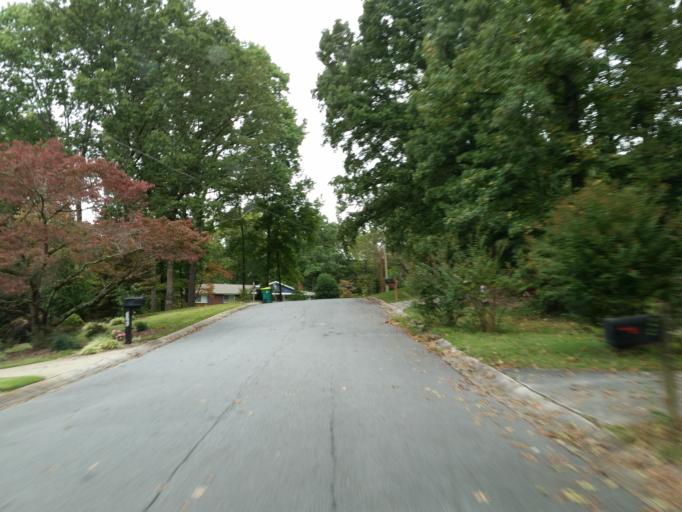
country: US
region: Georgia
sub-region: Cherokee County
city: Woodstock
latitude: 34.0337
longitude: -84.5110
